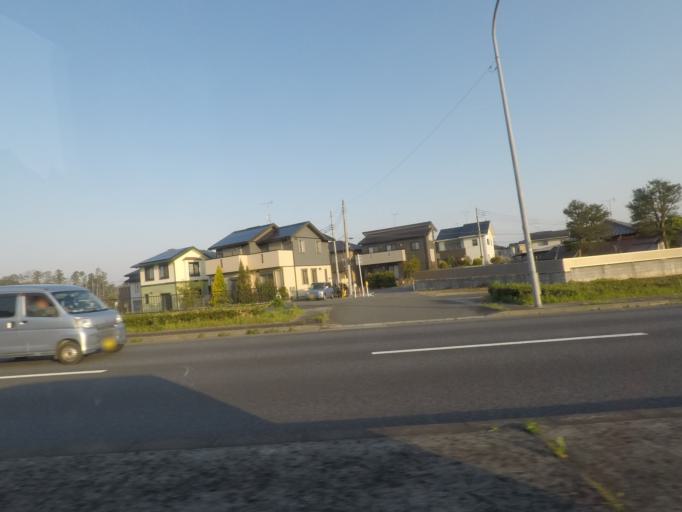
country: JP
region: Chiba
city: Shisui
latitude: 35.7221
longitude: 140.2666
